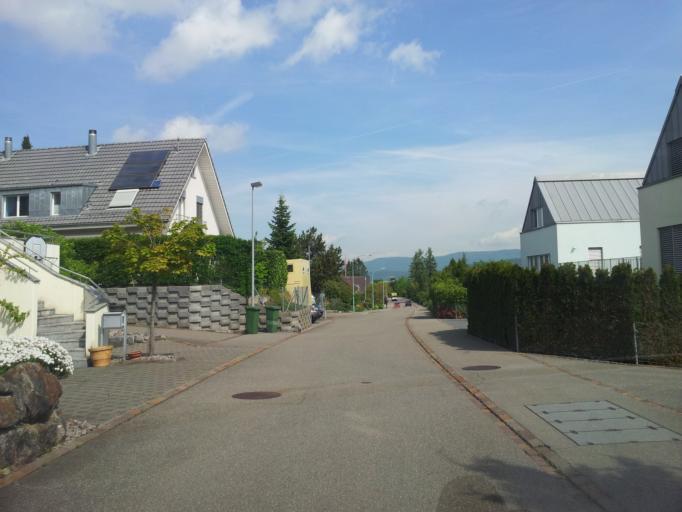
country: CH
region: Zurich
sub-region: Bezirk Dietikon
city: Dietikon / Oberdorf
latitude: 47.3981
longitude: 8.3867
